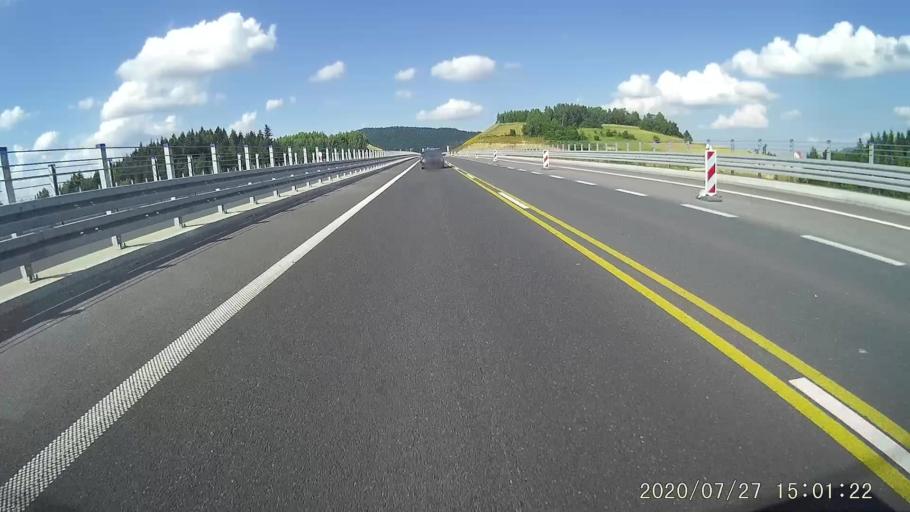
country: PL
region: Lesser Poland Voivodeship
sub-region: Powiat suski
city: Letownia
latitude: 49.6835
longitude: 19.8931
